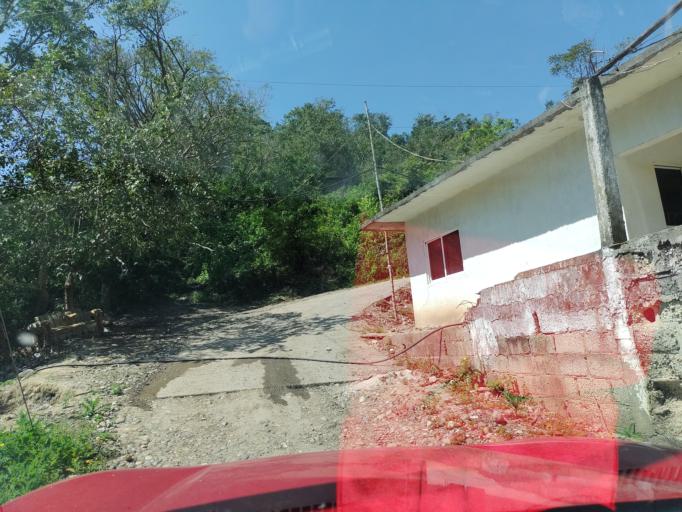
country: MX
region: Veracruz
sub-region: Papantla
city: Polutla
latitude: 20.4982
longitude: -97.2352
